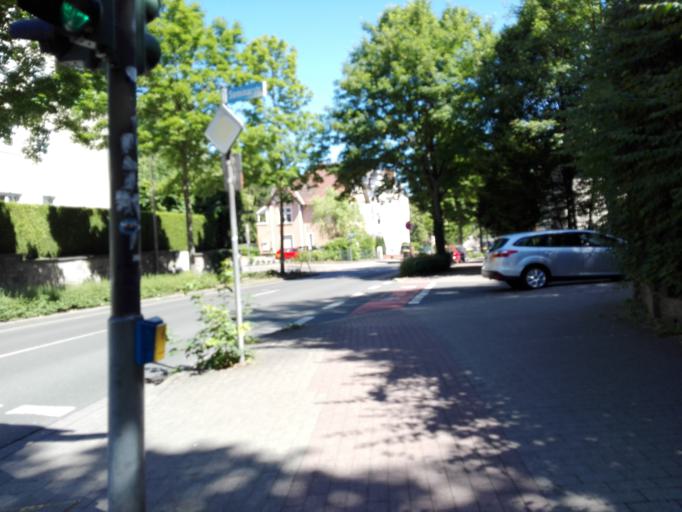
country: DE
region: North Rhine-Westphalia
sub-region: Regierungsbezirk Arnsberg
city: Unna
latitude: 51.5310
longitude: 7.6935
